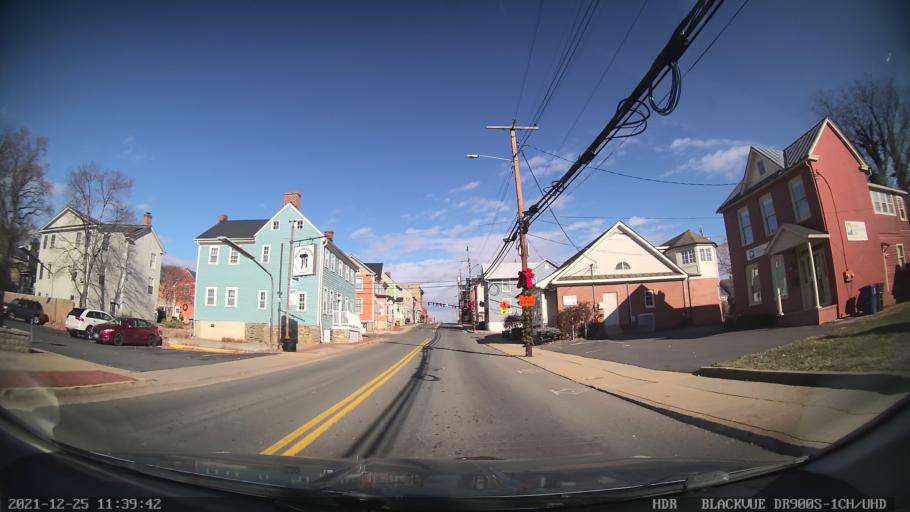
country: US
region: Virginia
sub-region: Loudoun County
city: Leesburg
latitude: 39.1132
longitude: -77.5656
